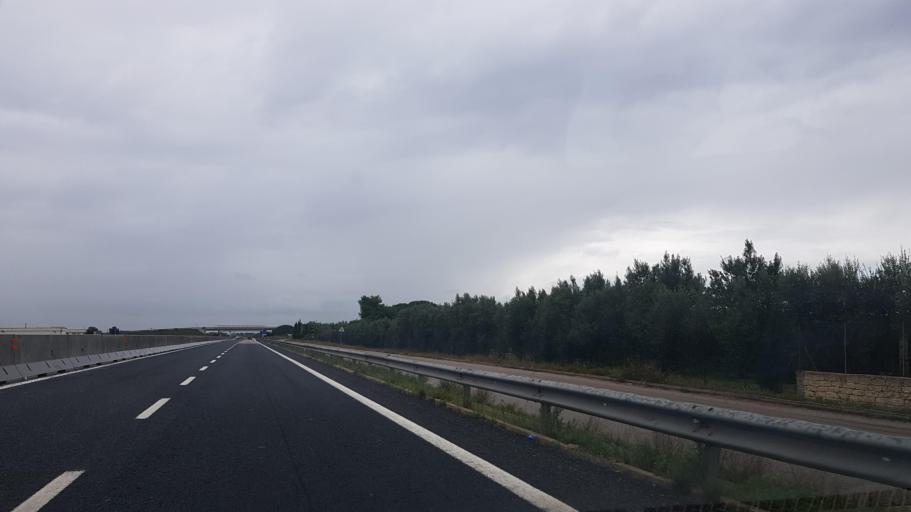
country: IT
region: Apulia
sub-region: Provincia di Taranto
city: Massafra
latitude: 40.5308
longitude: 17.0905
